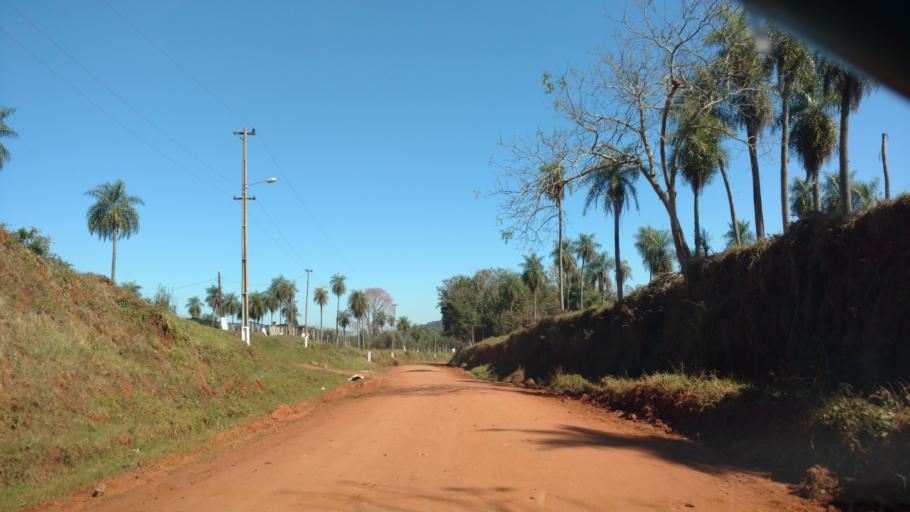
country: PY
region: Paraguari
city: Yaguaron
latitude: -25.5644
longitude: -57.3048
